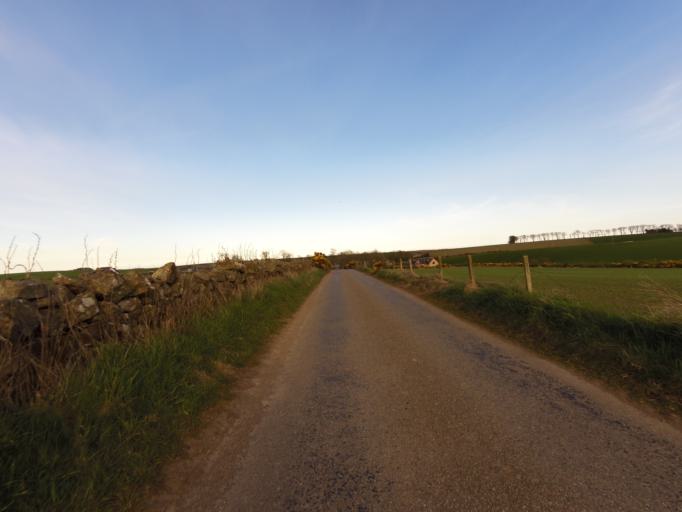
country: GB
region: Scotland
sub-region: Aberdeenshire
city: Stonehaven
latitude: 56.9126
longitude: -2.2245
